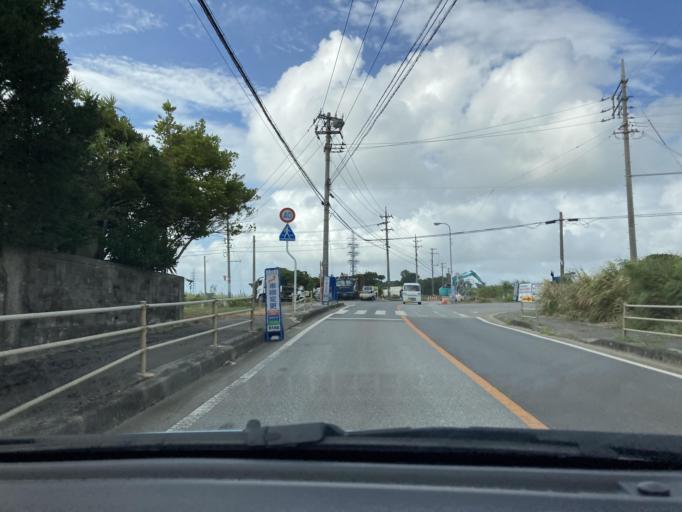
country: JP
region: Okinawa
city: Itoman
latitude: 26.1054
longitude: 127.6952
